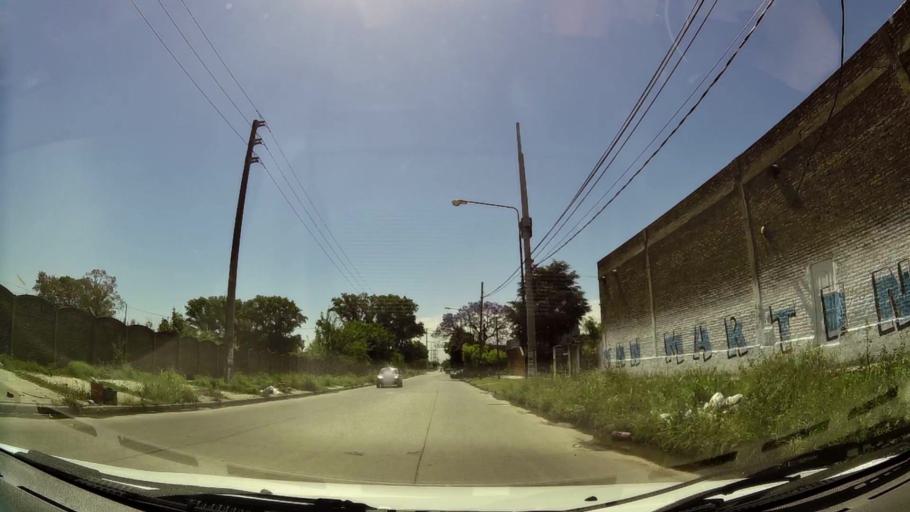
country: AR
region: Buenos Aires
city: Caseros
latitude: -34.5638
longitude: -58.5809
